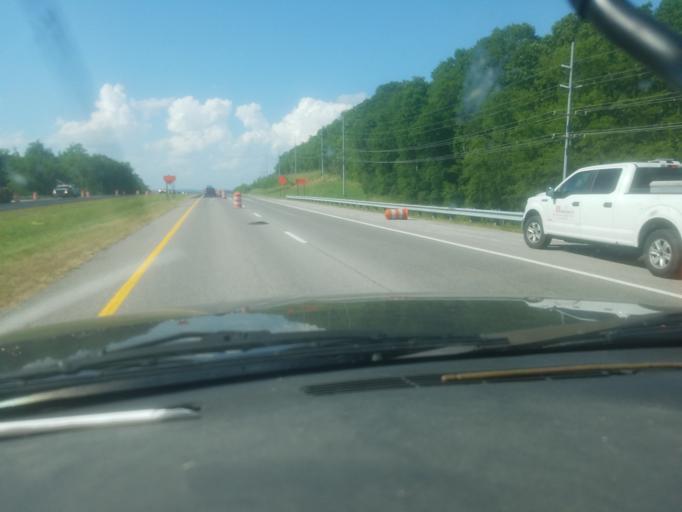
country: US
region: Tennessee
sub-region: Maury County
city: Mount Pleasant
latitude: 35.5355
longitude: -87.2215
